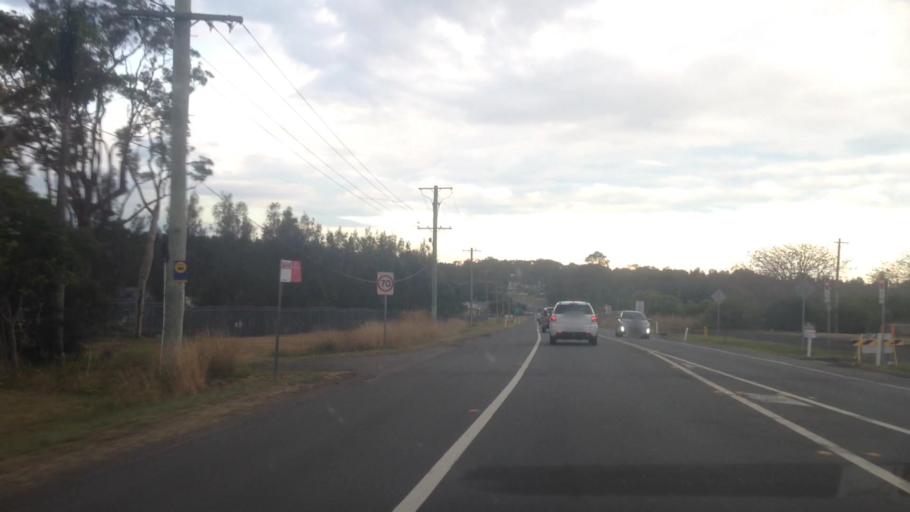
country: AU
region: New South Wales
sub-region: Wyong Shire
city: Tuggerawong
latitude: -33.2640
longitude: 151.4738
